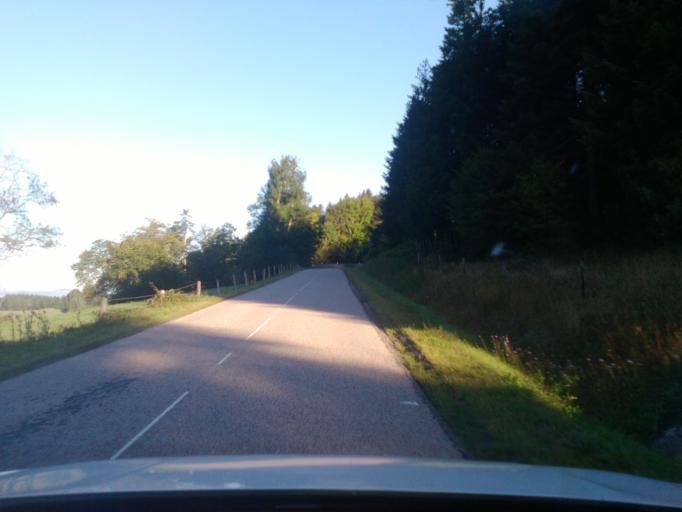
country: FR
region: Lorraine
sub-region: Departement des Vosges
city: Senones
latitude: 48.3363
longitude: 6.9933
